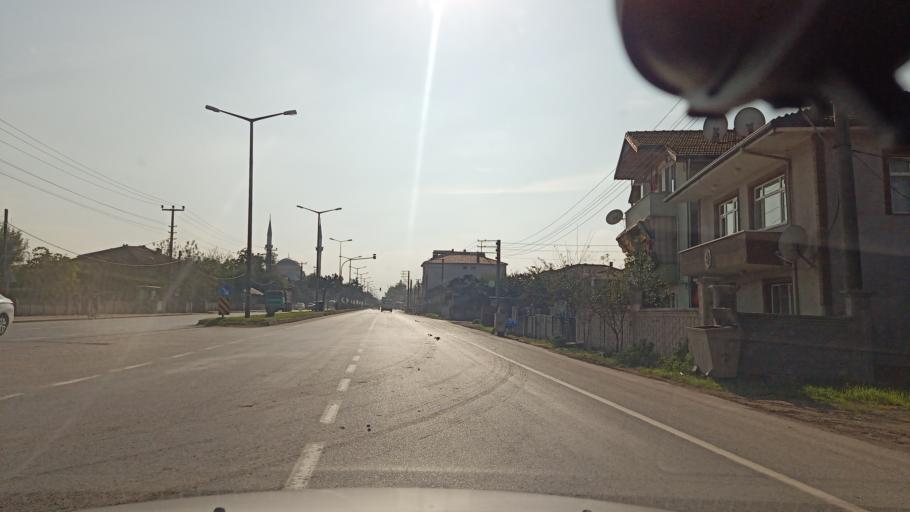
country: TR
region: Sakarya
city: Adapazari
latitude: 40.8114
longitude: 30.4051
